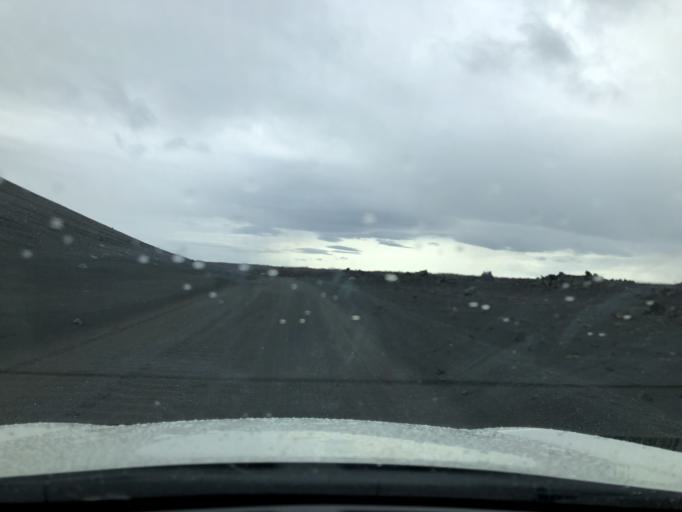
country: IS
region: Northeast
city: Laugar
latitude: 65.6099
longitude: -16.8845
